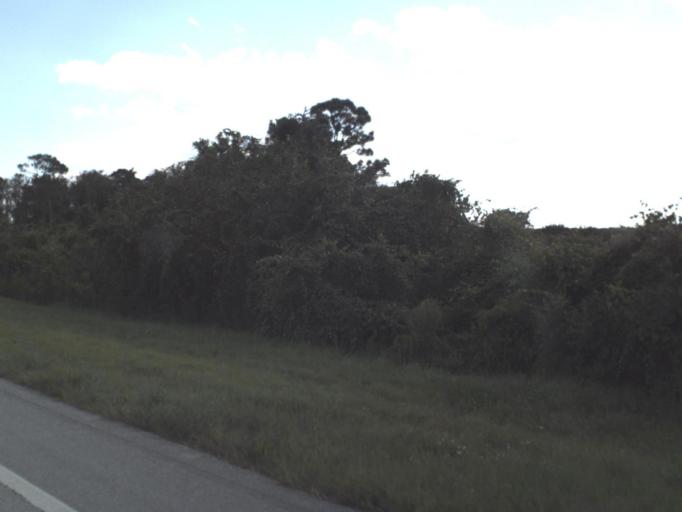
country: US
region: Florida
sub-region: Highlands County
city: Lake Placid
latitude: 27.3847
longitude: -81.1335
